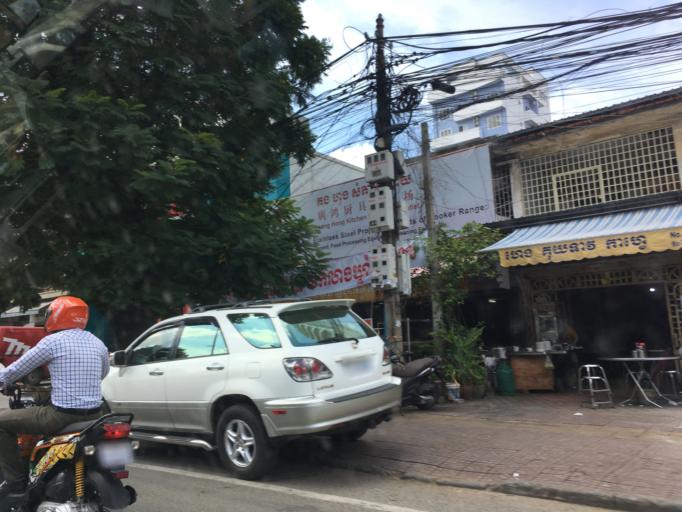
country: KH
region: Phnom Penh
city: Phnom Penh
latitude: 11.5438
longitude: 104.9144
